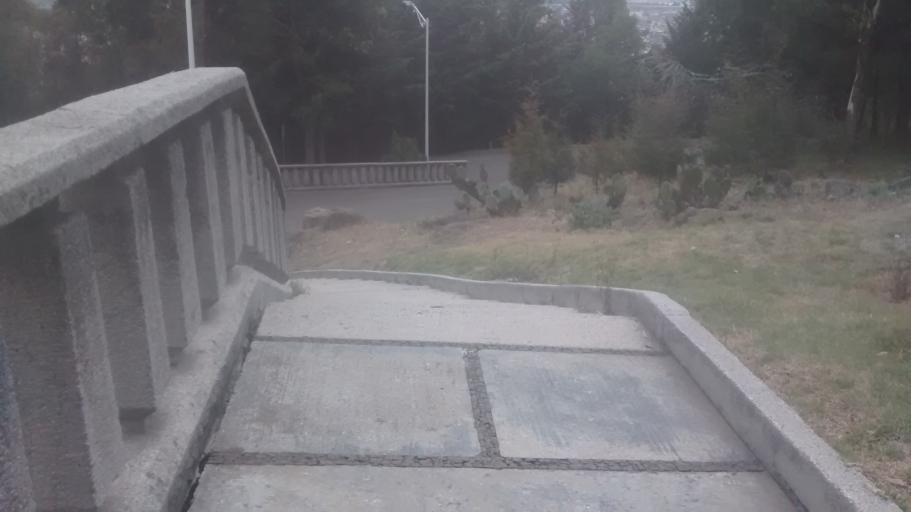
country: MX
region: Mexico
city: San Buenaventura
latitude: 19.2839
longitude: -99.6778
